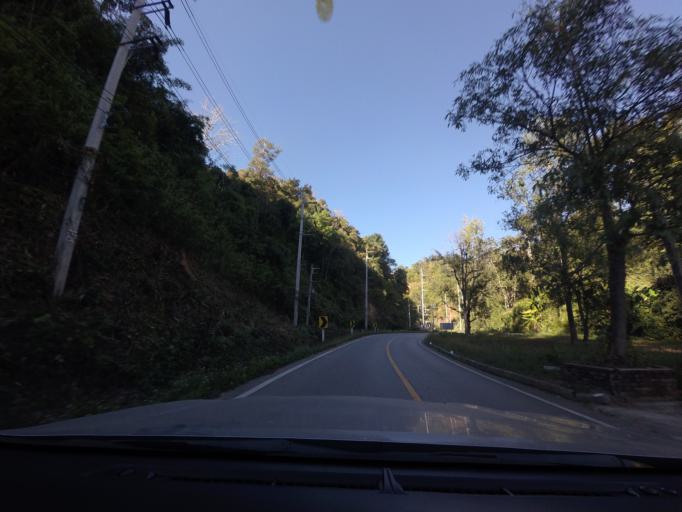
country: TH
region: Mae Hong Son
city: Mae Hi
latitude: 19.2092
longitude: 98.6703
